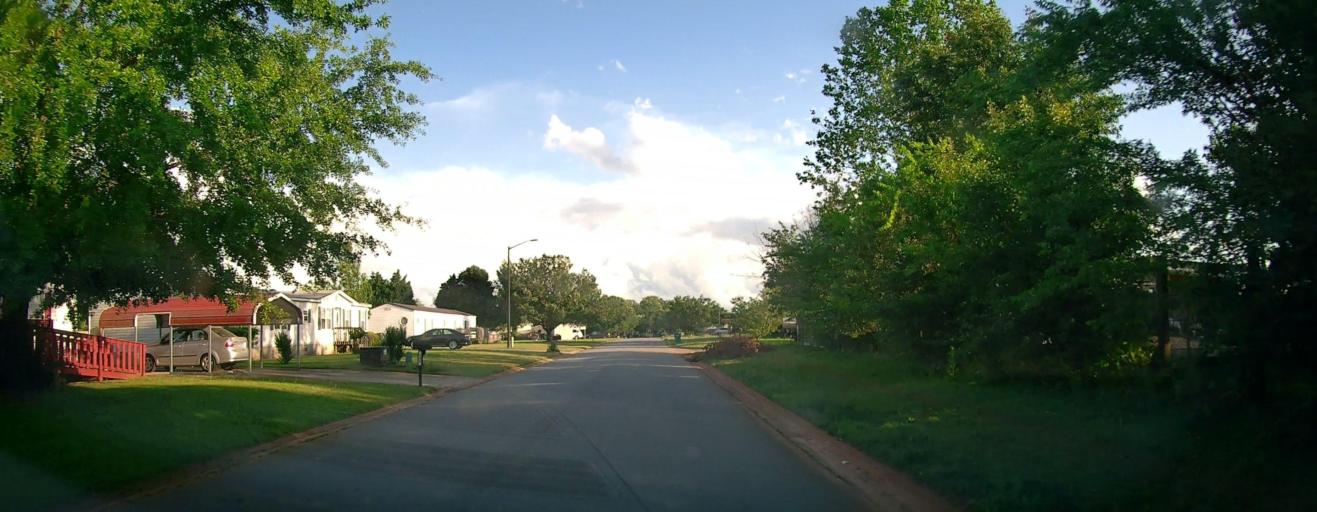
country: US
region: Georgia
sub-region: Houston County
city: Centerville
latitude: 32.6401
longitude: -83.7241
